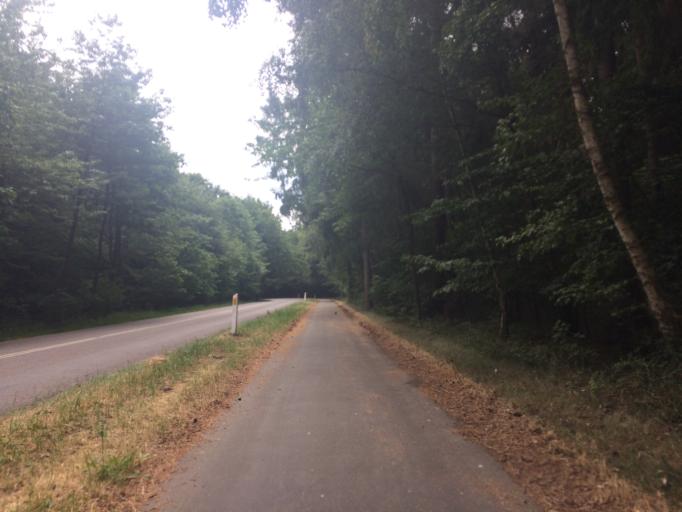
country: DK
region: Capital Region
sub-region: Bornholm Kommune
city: Ronne
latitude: 55.1587
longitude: 14.7151
